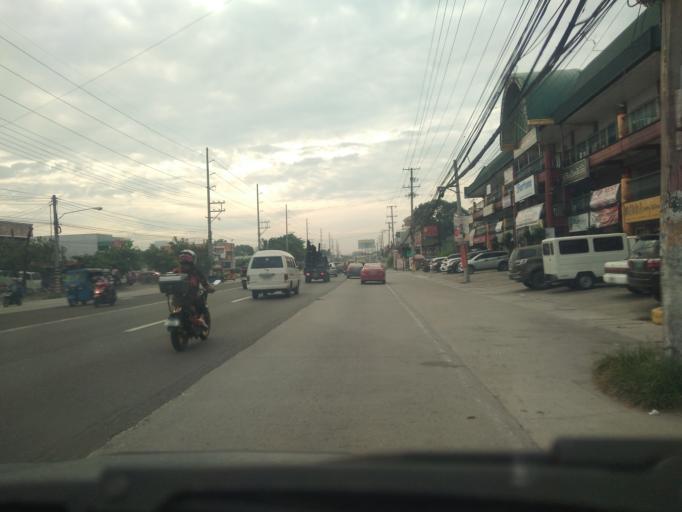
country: PH
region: Central Luzon
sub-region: Province of Pampanga
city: Magliman
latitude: 15.0520
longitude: 120.6631
